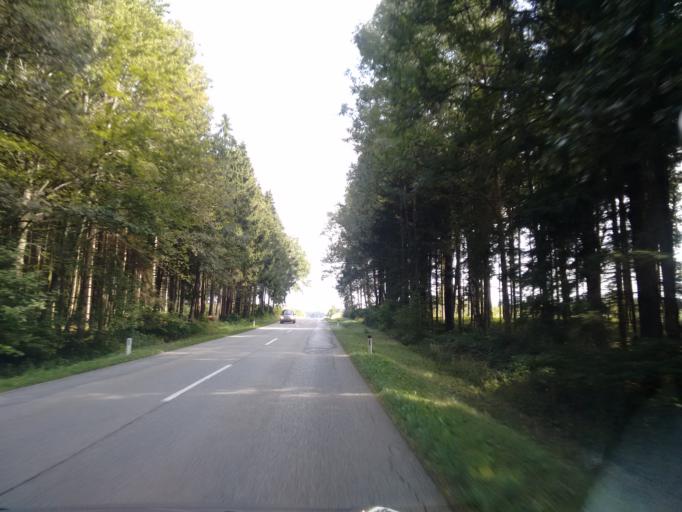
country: AT
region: Upper Austria
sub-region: Wels-Land
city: Thalheim bei Wels
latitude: 48.1284
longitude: 14.0820
